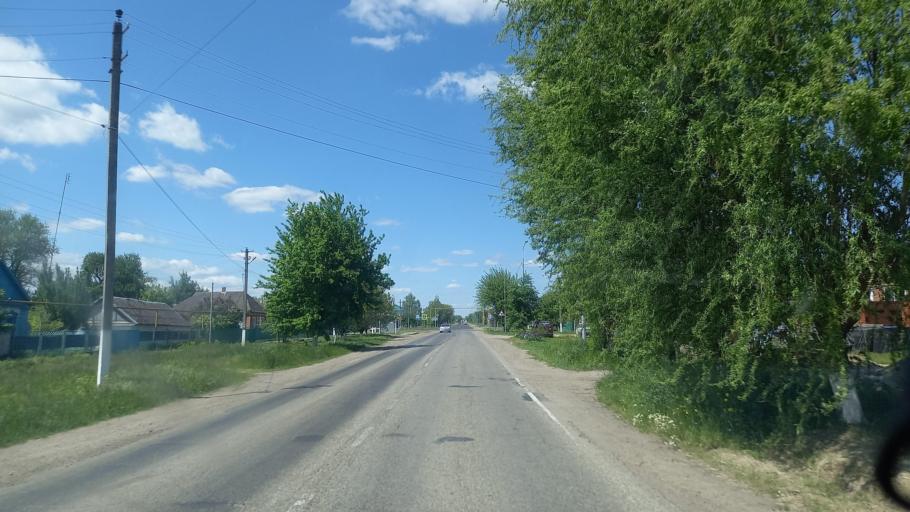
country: RU
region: Krasnodarskiy
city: Tbilisskaya
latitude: 45.3266
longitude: 40.2611
